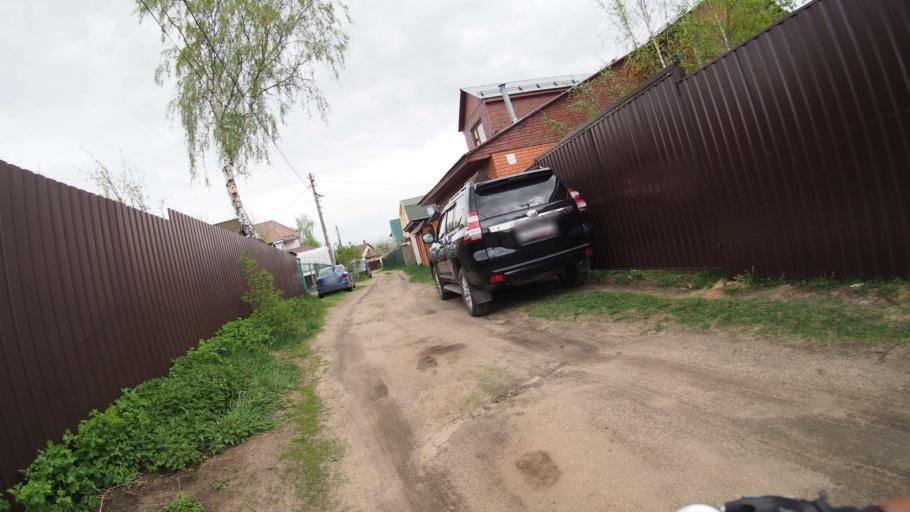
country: RU
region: Moskovskaya
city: Ramenskoye
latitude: 55.5582
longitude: 38.2341
